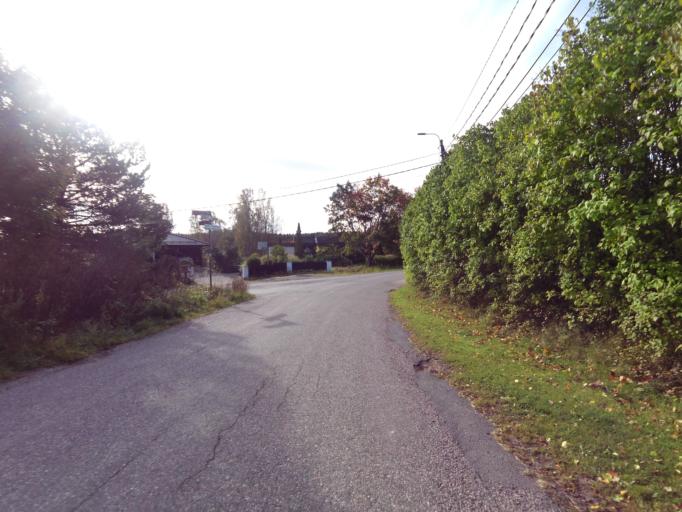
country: FI
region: Uusimaa
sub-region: Helsinki
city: Koukkuniemi
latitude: 60.1416
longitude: 24.6911
